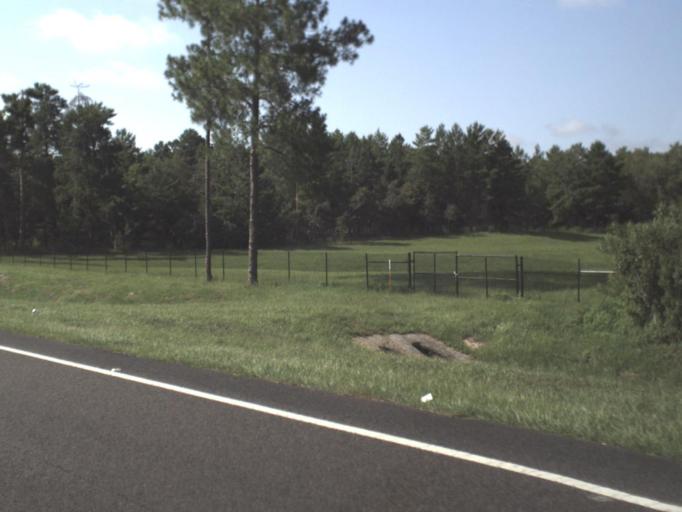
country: US
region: Florida
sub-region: Citrus County
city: Sugarmill Woods
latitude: 28.6823
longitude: -82.4917
